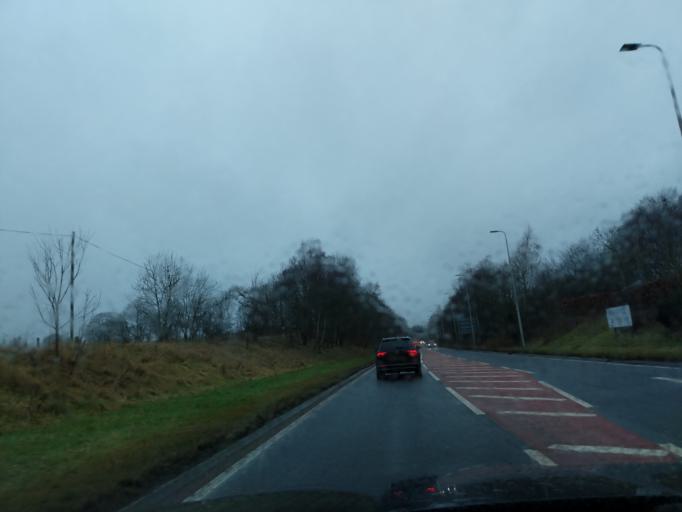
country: GB
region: Scotland
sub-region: The Scottish Borders
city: Melrose
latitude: 55.5989
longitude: -2.7460
